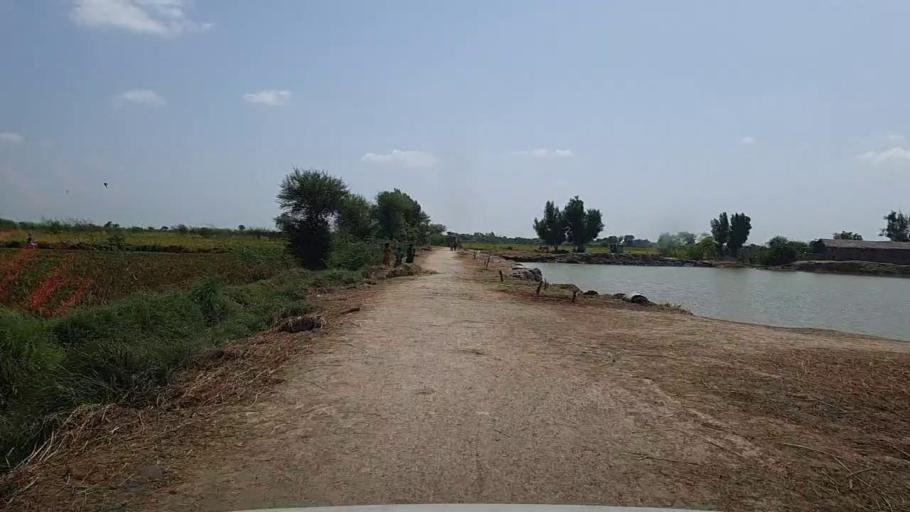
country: PK
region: Sindh
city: Kario
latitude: 24.6389
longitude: 68.5719
